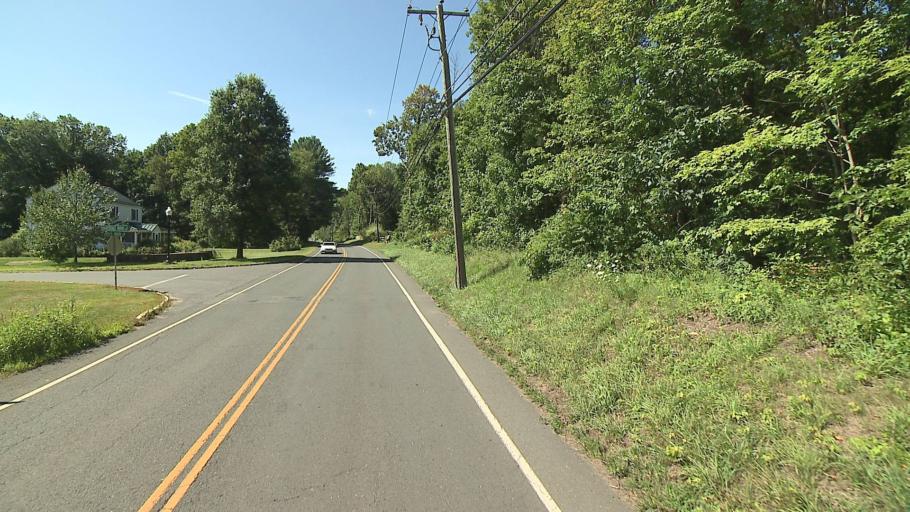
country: US
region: Connecticut
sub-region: Hartford County
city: Tariffville
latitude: 41.9281
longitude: -72.7341
